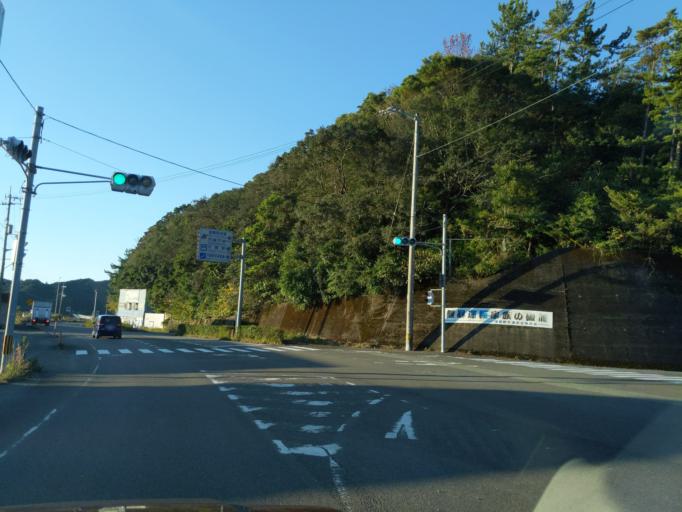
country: JP
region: Kochi
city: Muroto-misakicho
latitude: 33.5718
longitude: 134.3082
